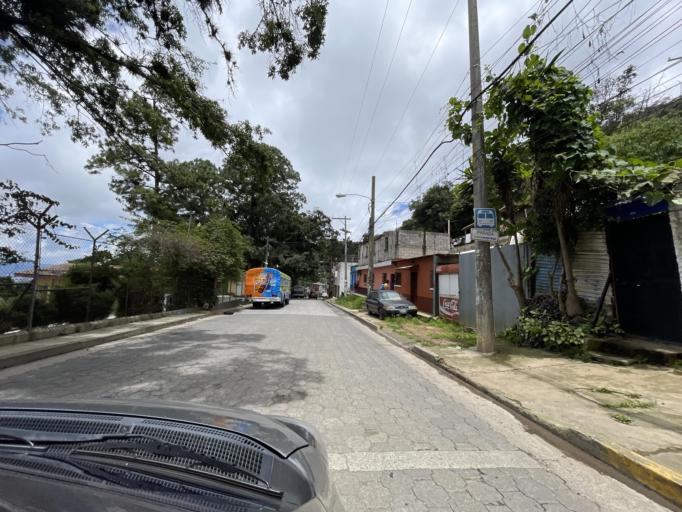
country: GT
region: Guatemala
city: Mixco
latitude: 14.6386
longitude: -90.6207
